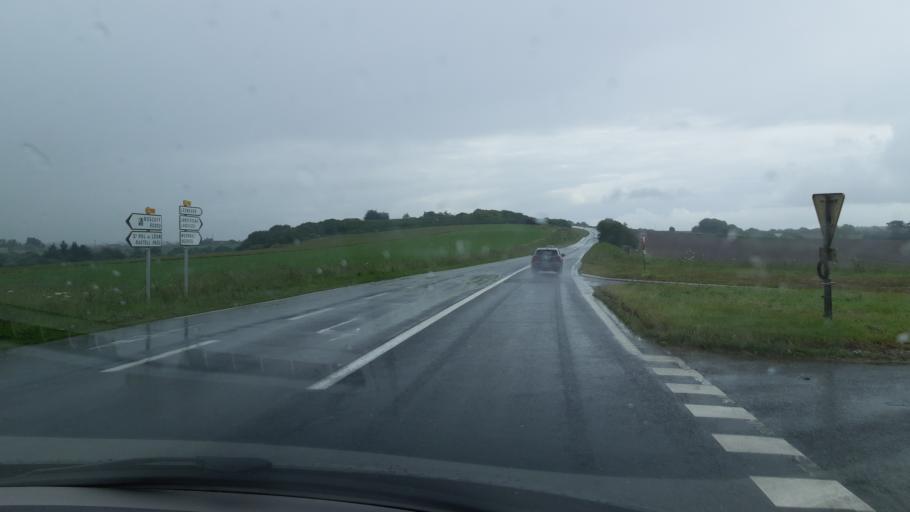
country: FR
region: Brittany
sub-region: Departement du Finistere
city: Plougoulm
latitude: 48.6481
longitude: -4.0431
